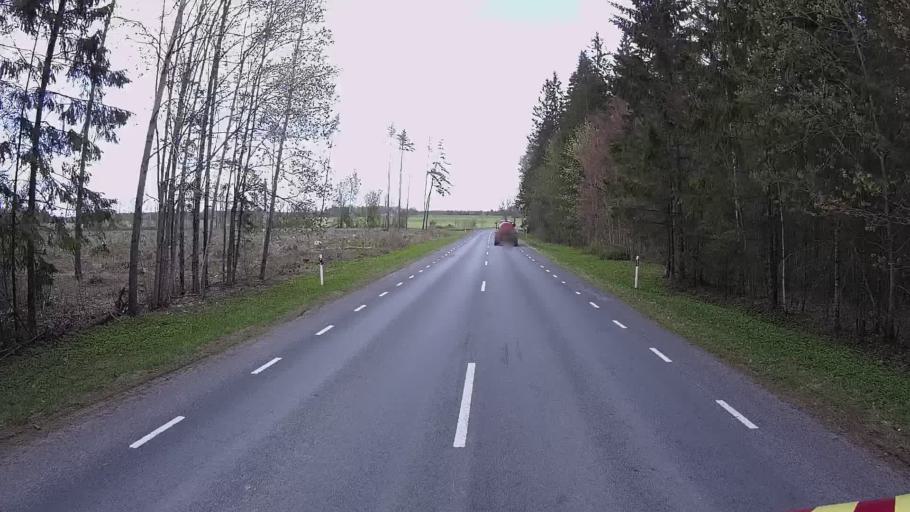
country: EE
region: Jaervamaa
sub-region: Koeru vald
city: Koeru
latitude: 58.9720
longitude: 26.0352
